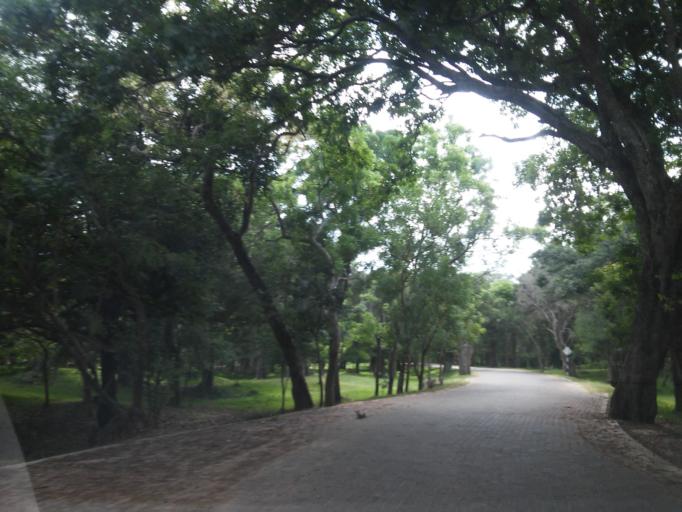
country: LK
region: North Central
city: Anuradhapura
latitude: 8.3712
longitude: 80.4004
